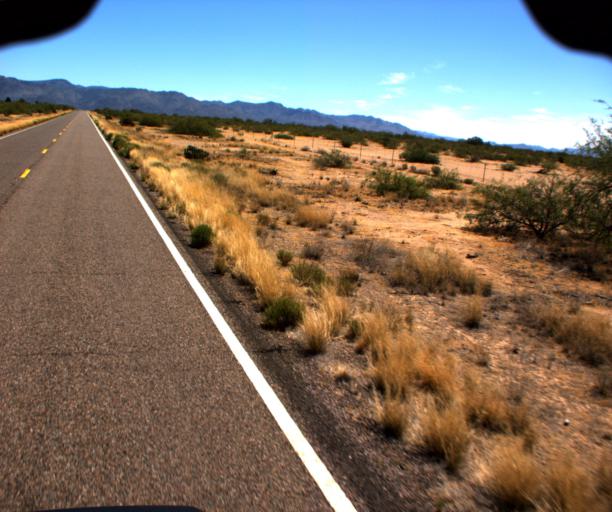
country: US
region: Arizona
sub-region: Yavapai County
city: Congress
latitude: 34.1500
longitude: -112.8836
